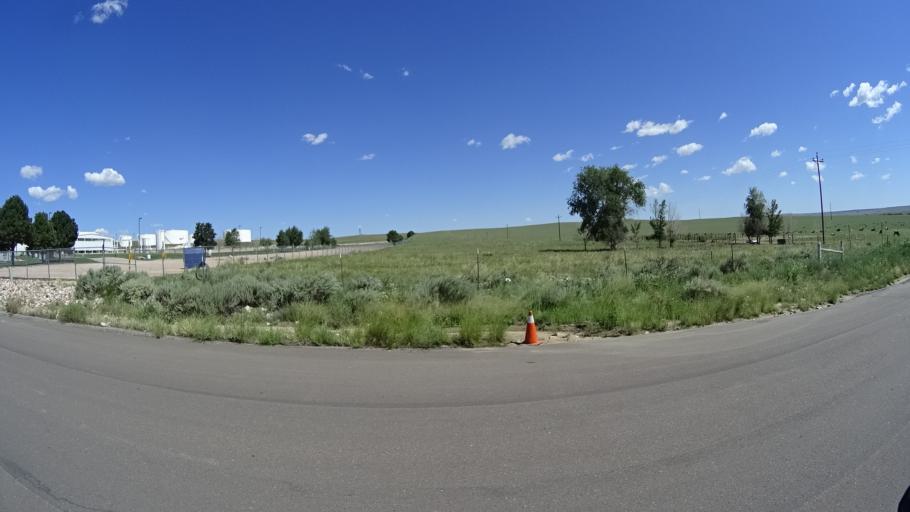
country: US
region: Colorado
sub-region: El Paso County
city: Security-Widefield
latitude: 38.7809
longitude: -104.6741
